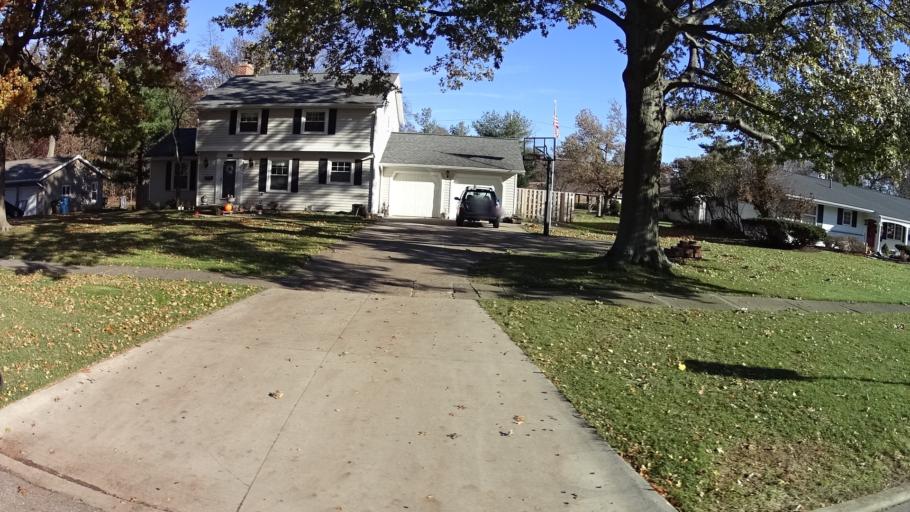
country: US
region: Ohio
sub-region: Lorain County
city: Avon Lake
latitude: 41.5109
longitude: -82.0007
